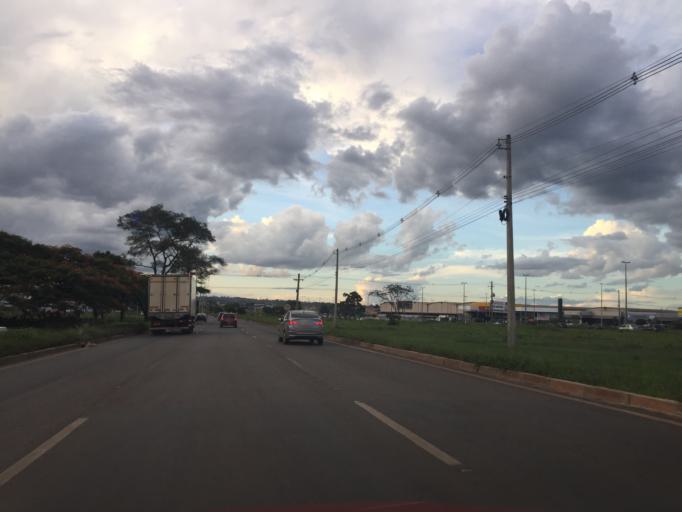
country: BR
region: Federal District
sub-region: Brasilia
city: Brasilia
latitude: -15.7929
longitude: -47.9770
